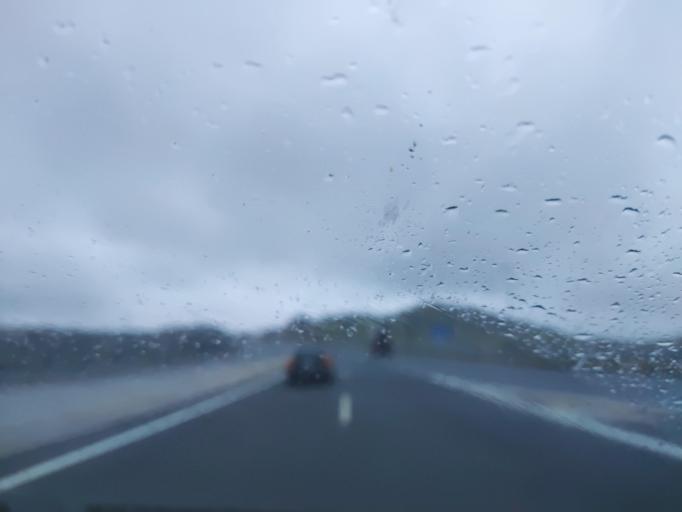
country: ES
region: Castille-La Mancha
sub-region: Province of Toledo
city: Toledo
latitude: 39.8644
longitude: -4.0927
